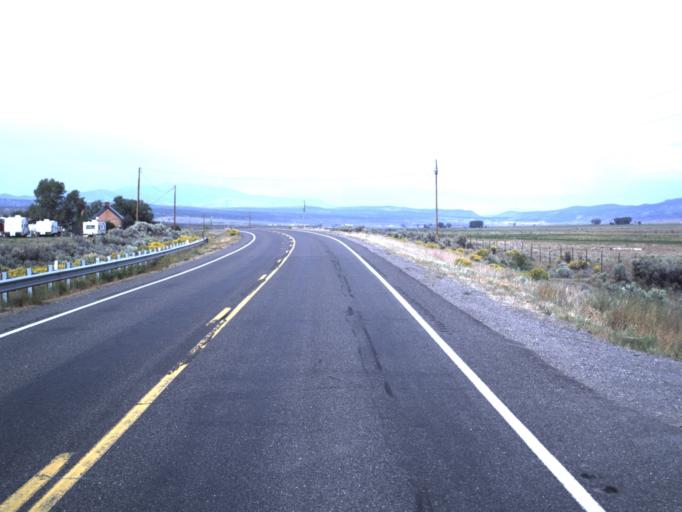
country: US
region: Utah
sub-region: Garfield County
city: Panguitch
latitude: 37.9160
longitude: -112.4275
